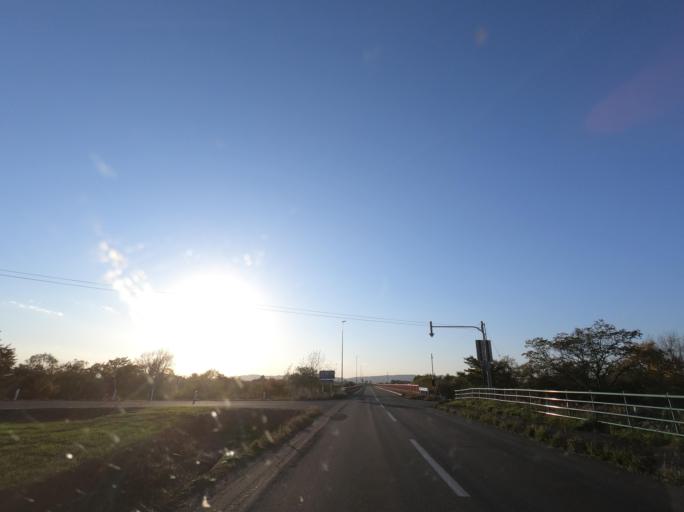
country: JP
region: Hokkaido
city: Iwamizawa
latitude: 42.9786
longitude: 141.8623
